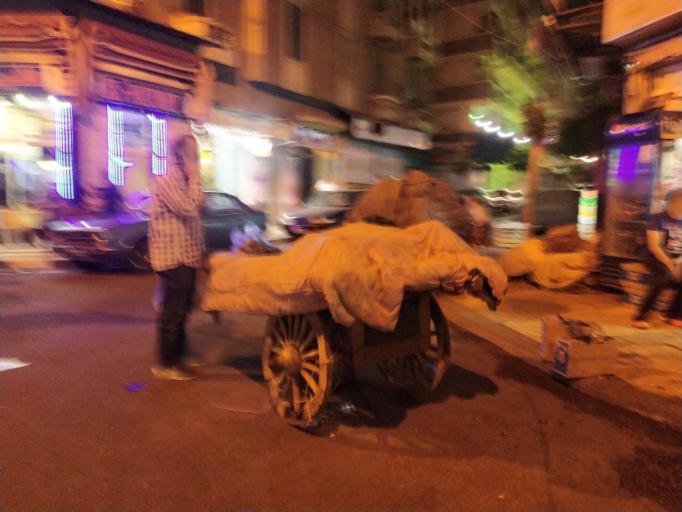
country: EG
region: Alexandria
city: Alexandria
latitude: 31.2123
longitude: 29.9255
